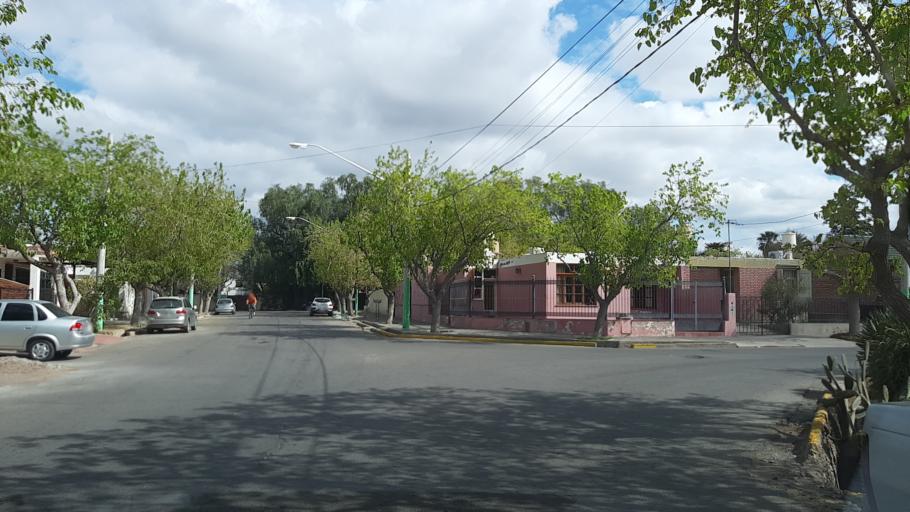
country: AR
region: San Juan
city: San Juan
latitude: -31.5315
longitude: -68.5907
